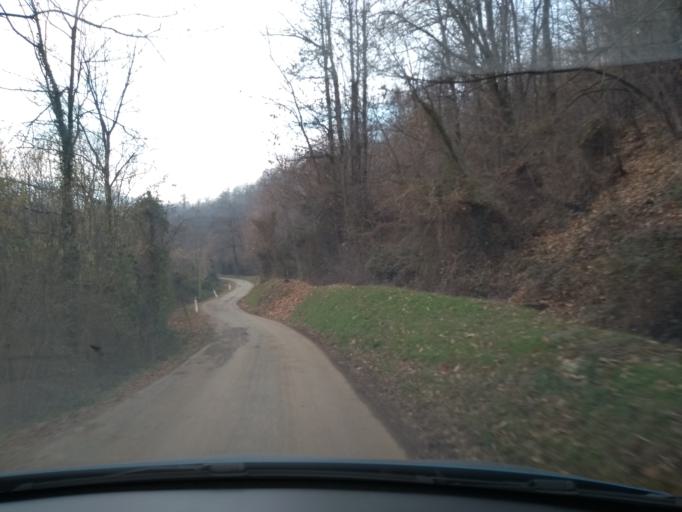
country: IT
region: Piedmont
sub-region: Provincia di Torino
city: Balangero
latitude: 45.2703
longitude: 7.5346
